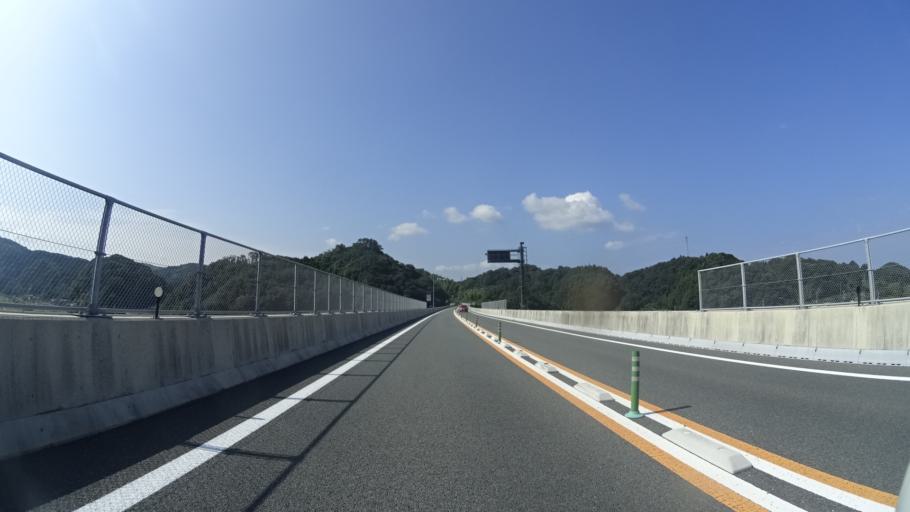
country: JP
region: Shimane
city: Gotsucho
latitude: 35.0734
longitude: 132.3324
